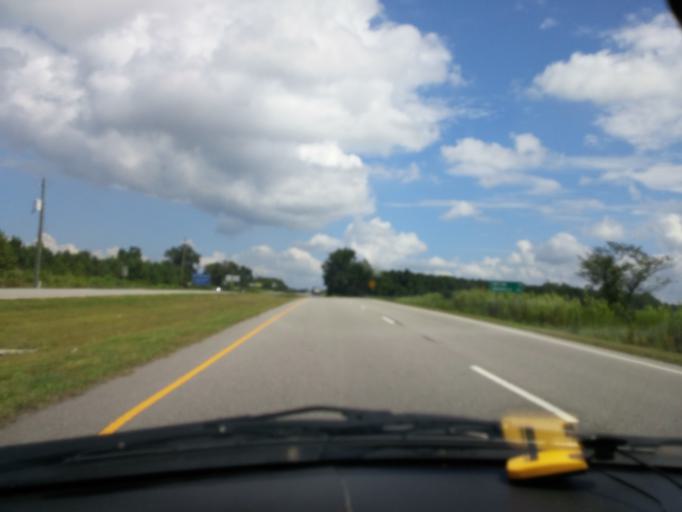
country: US
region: North Carolina
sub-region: Lenoir County
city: Kinston
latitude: 35.2975
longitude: -77.5379
